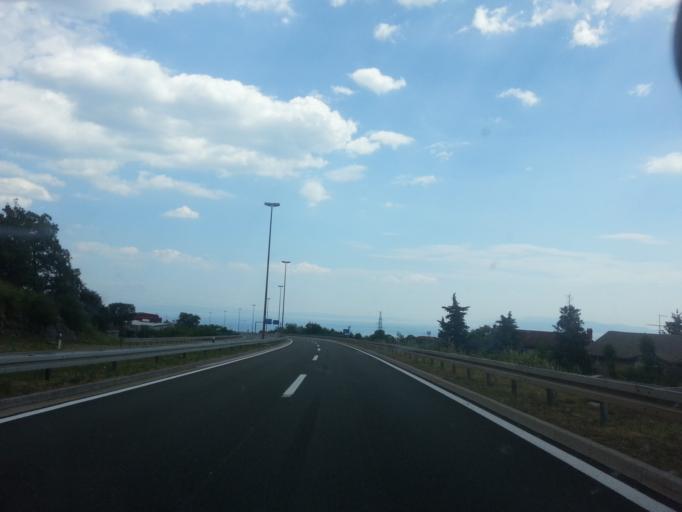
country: HR
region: Primorsko-Goranska
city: Matulji
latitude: 45.3693
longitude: 14.3267
